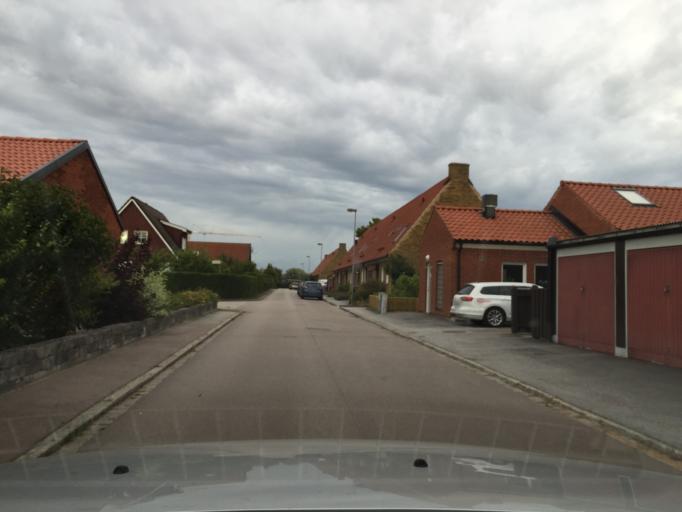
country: SE
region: Skane
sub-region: Burlovs Kommun
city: Arloev
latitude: 55.6007
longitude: 13.0814
